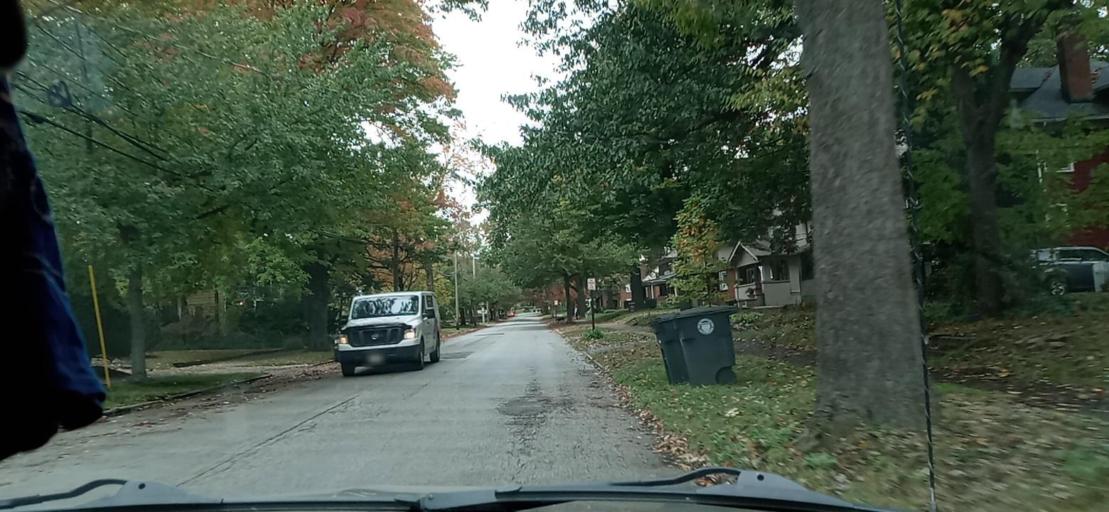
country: US
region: Ohio
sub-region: Summit County
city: Akron
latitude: 41.0868
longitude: -81.5342
